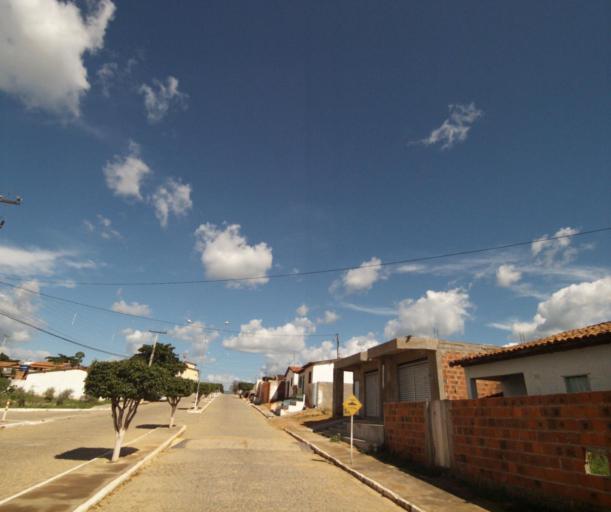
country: BR
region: Bahia
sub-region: Pocoes
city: Pocoes
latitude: -14.2416
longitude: -40.7683
